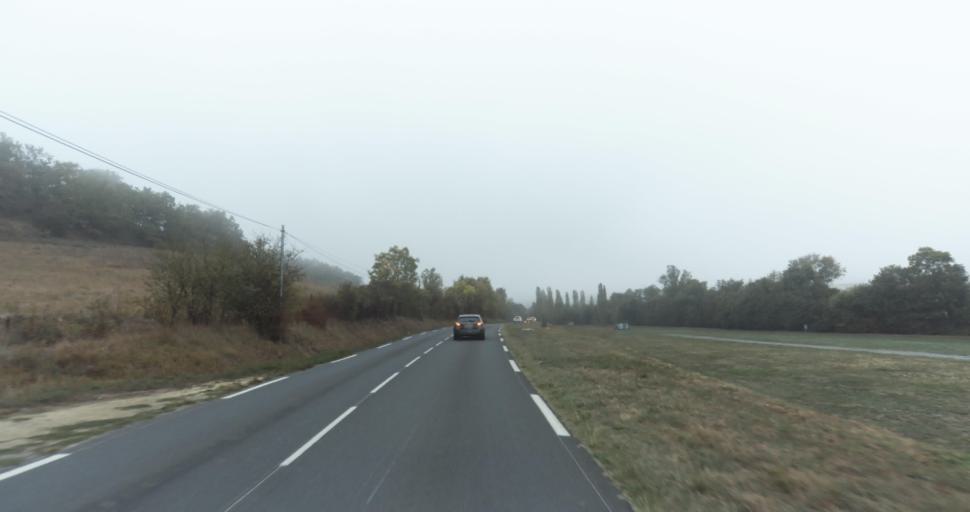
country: FR
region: Midi-Pyrenees
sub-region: Departement du Gers
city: Auch
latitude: 43.6697
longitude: 0.6204
